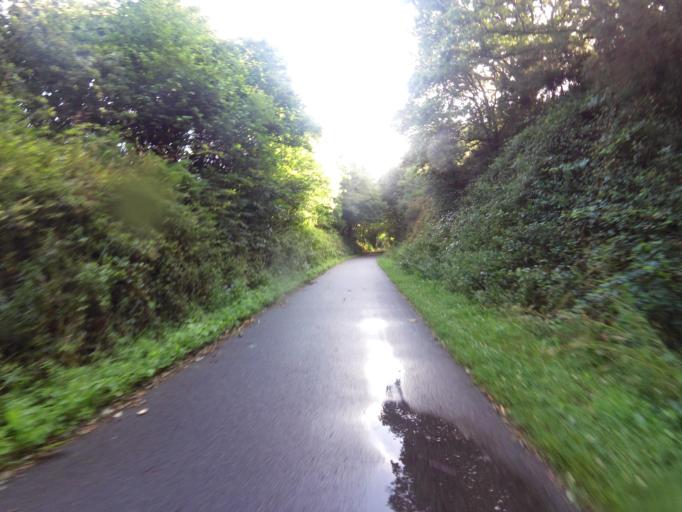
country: FR
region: Brittany
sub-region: Departement du Morbihan
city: Guillac
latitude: 47.9108
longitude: -2.4311
